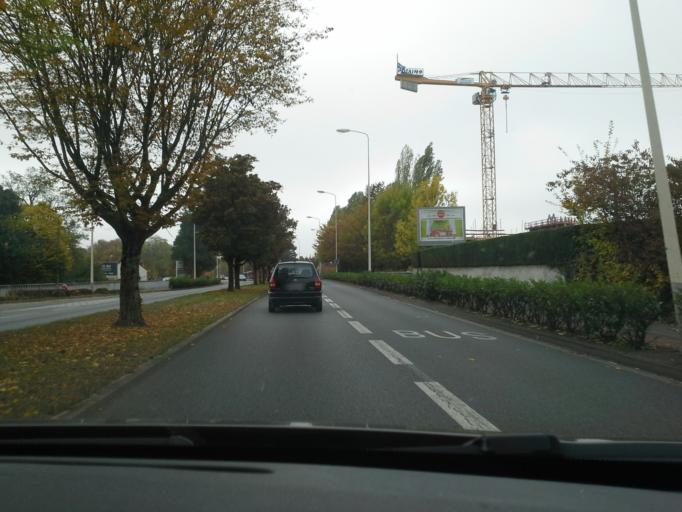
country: FR
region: Centre
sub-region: Departement d'Indre-et-Loire
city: Tours
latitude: 47.4144
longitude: 0.7031
